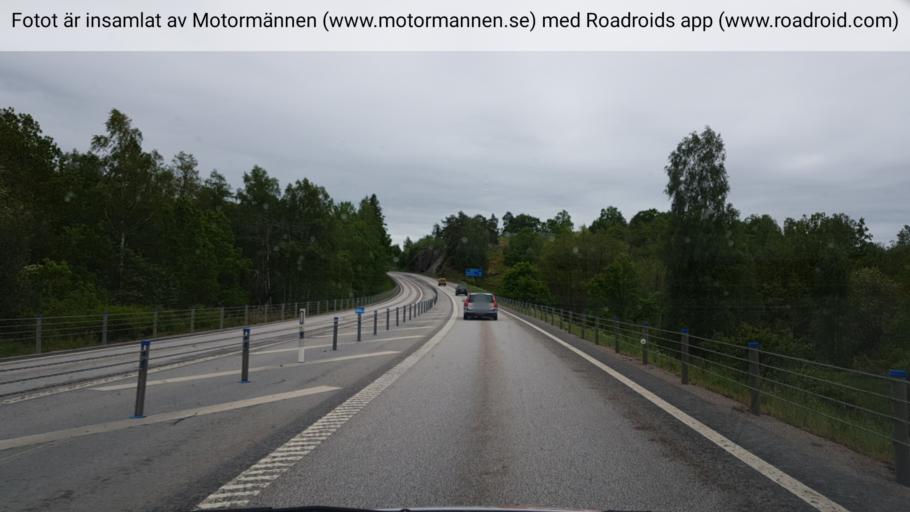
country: SE
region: Kalmar
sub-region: Vasterviks Kommun
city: Gamleby
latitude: 57.8870
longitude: 16.3868
